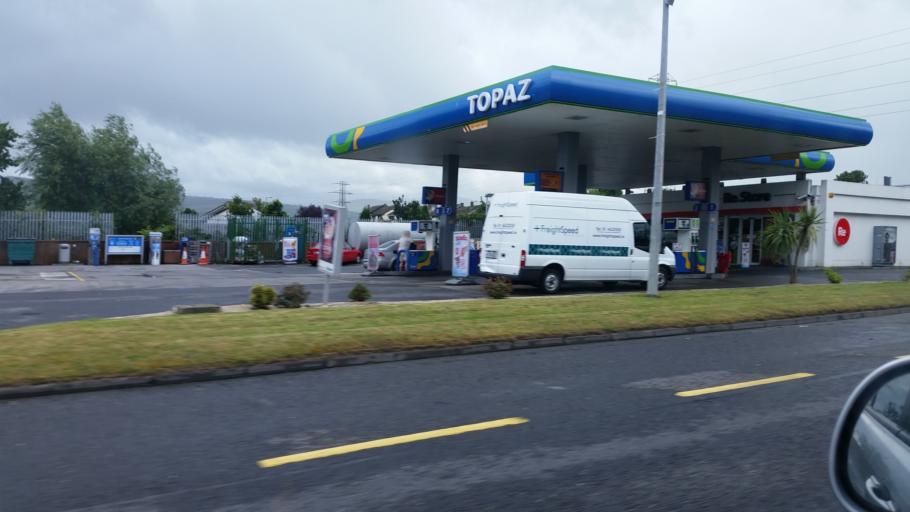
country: IE
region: Leinster
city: Firhouse
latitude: 53.2872
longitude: -6.3455
